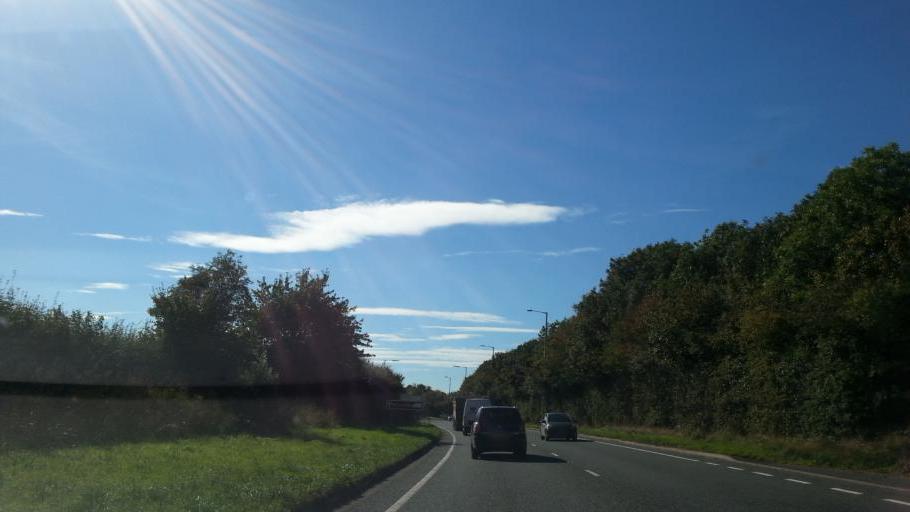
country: GB
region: England
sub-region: Telford and Wrekin
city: Newport
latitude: 52.7608
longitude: -2.3672
